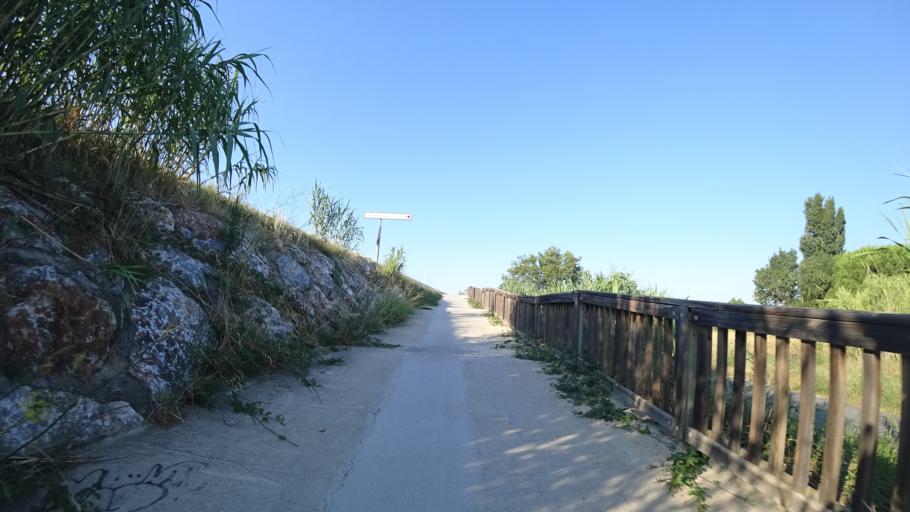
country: FR
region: Languedoc-Roussillon
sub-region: Departement des Pyrenees-Orientales
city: Canet-en-Roussillon
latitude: 42.7122
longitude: 3.0241
